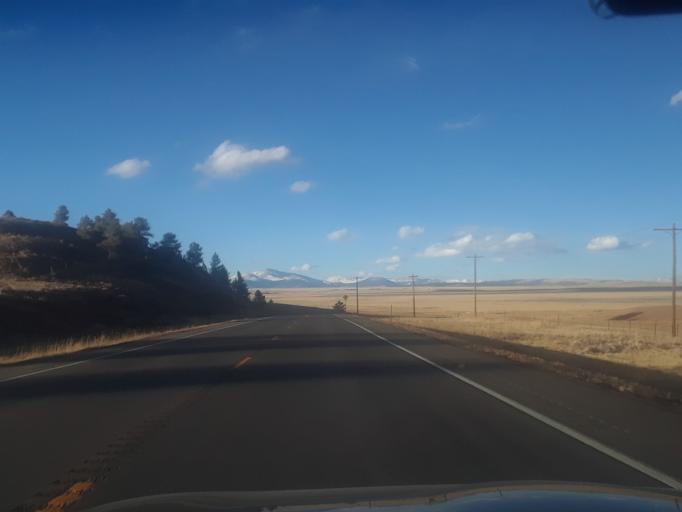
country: US
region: Colorado
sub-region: Chaffee County
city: Buena Vista
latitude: 38.9932
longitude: -105.9595
